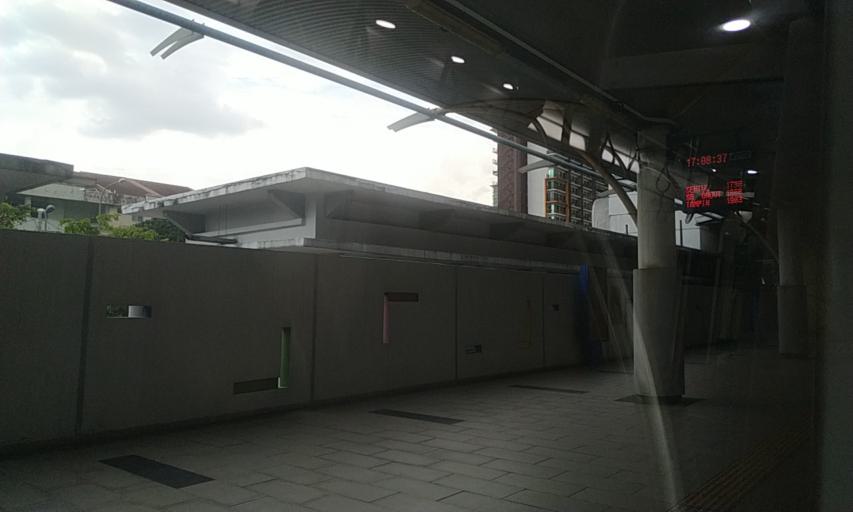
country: MY
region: Kuala Lumpur
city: Kuala Lumpur
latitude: 3.2149
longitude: 101.6723
